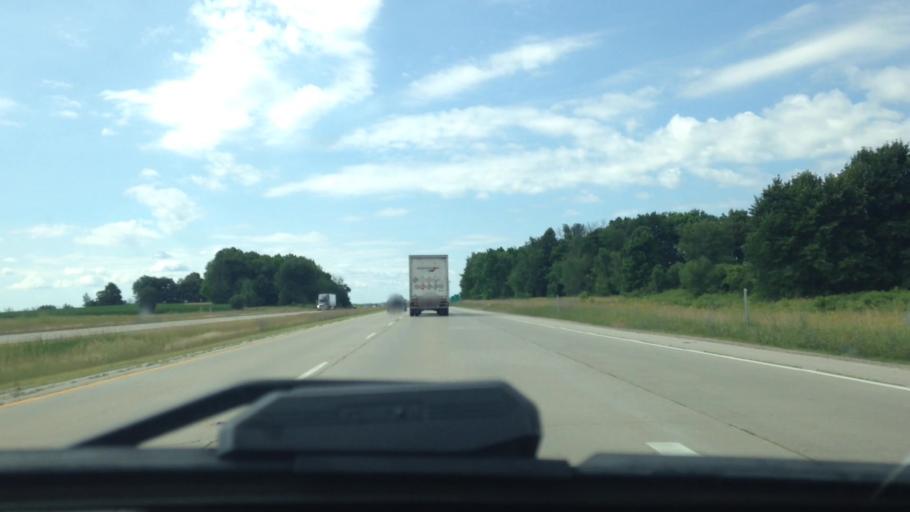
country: US
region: Wisconsin
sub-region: Washington County
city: Jackson
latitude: 43.3485
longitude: -88.1911
